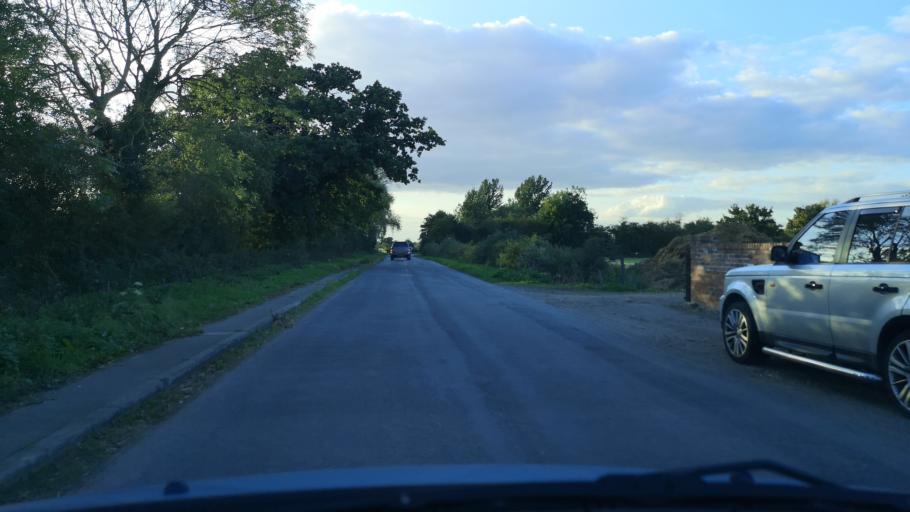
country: GB
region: England
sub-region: Doncaster
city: Stainforth
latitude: 53.6257
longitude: -1.0162
